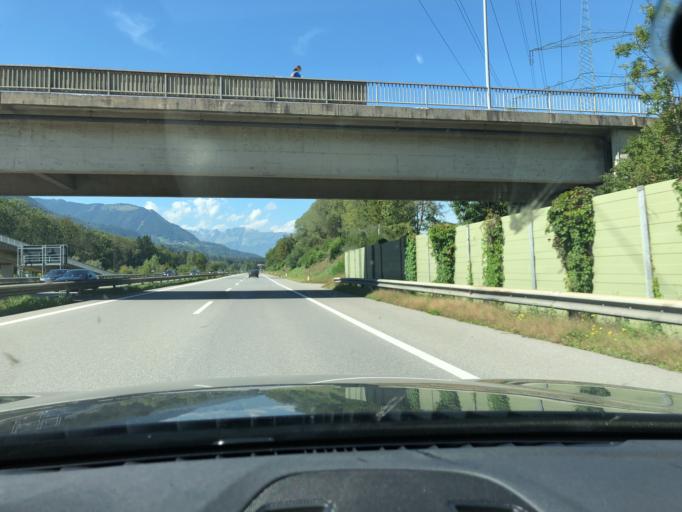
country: AT
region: Vorarlberg
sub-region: Politischer Bezirk Feldkirch
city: Schlins
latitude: 47.1975
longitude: 9.6920
